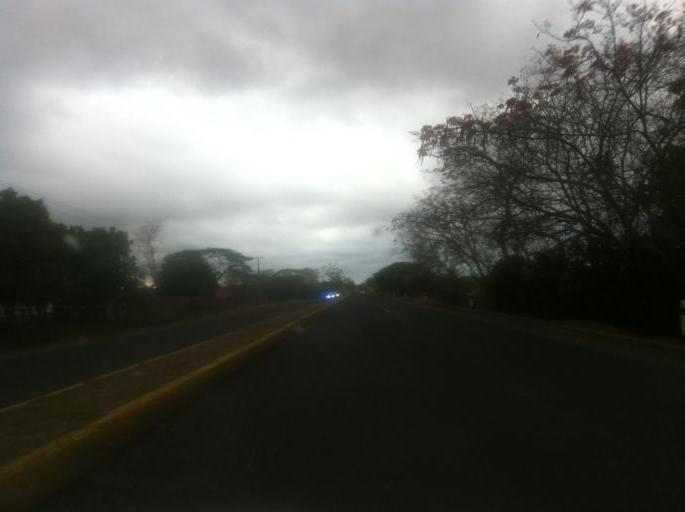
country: NI
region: Granada
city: Granada
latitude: 11.9449
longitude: -85.9805
